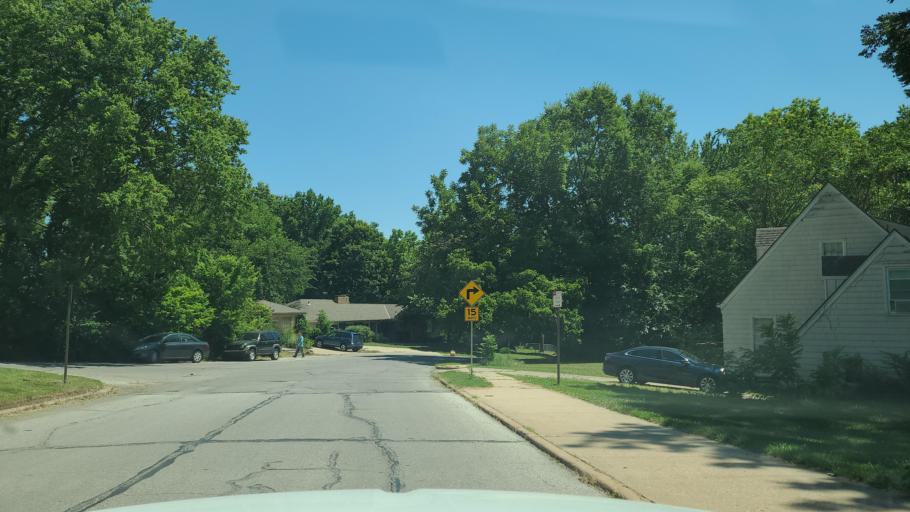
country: US
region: Kansas
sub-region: Douglas County
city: Lawrence
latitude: 38.9544
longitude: -95.2433
